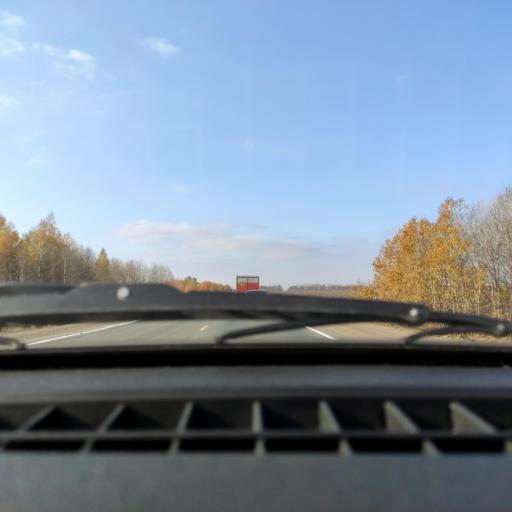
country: RU
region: Bashkortostan
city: Iglino
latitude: 54.7350
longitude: 56.2758
